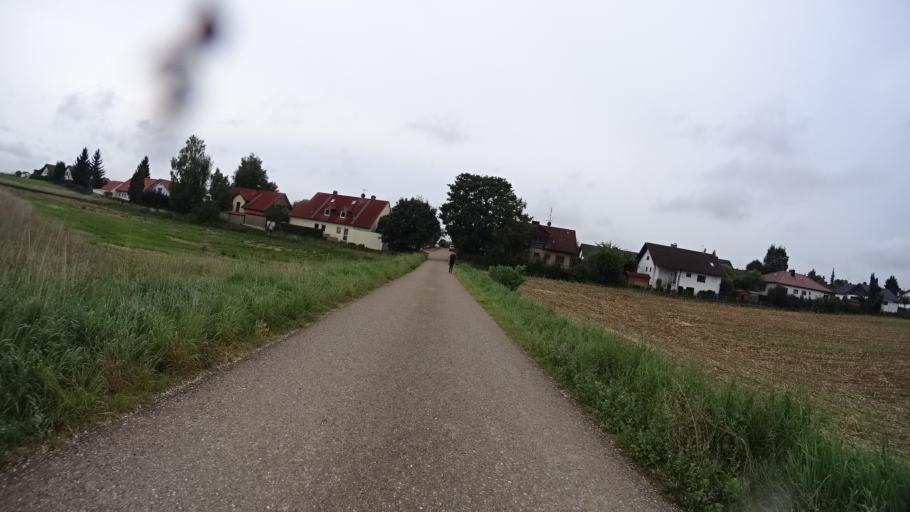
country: DE
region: Bavaria
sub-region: Upper Bavaria
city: Bohmfeld
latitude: 48.8390
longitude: 11.3556
